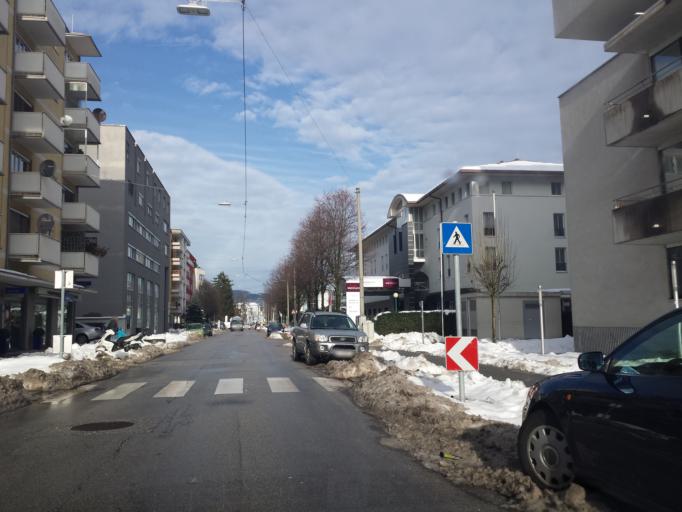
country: AT
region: Salzburg
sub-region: Salzburg Stadt
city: Salzburg
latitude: 47.8092
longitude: 13.0508
